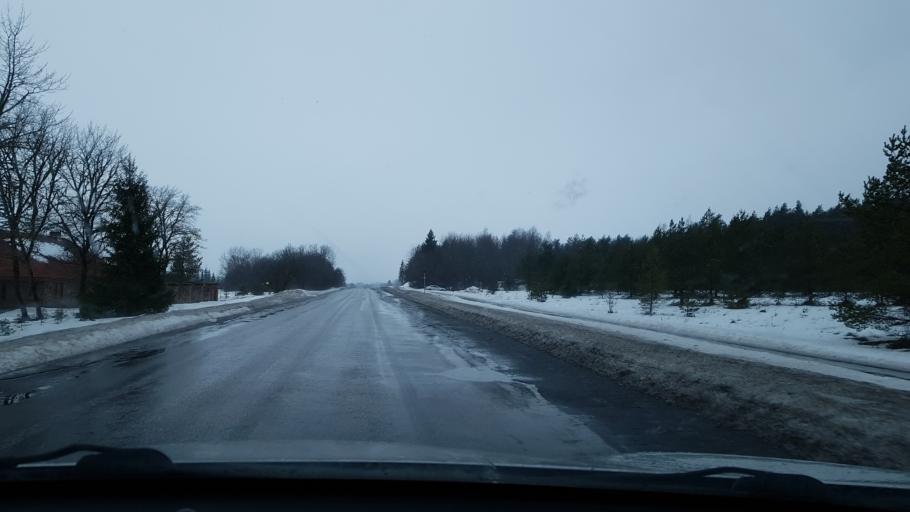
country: EE
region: Raplamaa
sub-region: Kohila vald
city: Kohila
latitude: 59.1654
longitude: 24.6945
